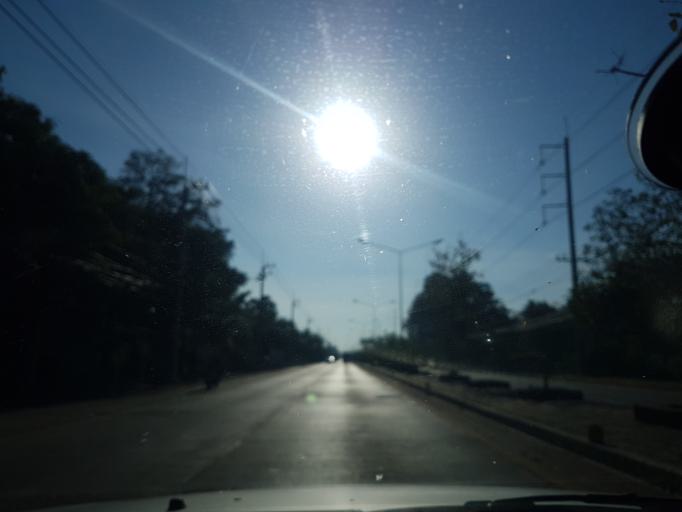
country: TH
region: Lop Buri
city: Lop Buri
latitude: 14.7683
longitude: 100.7080
